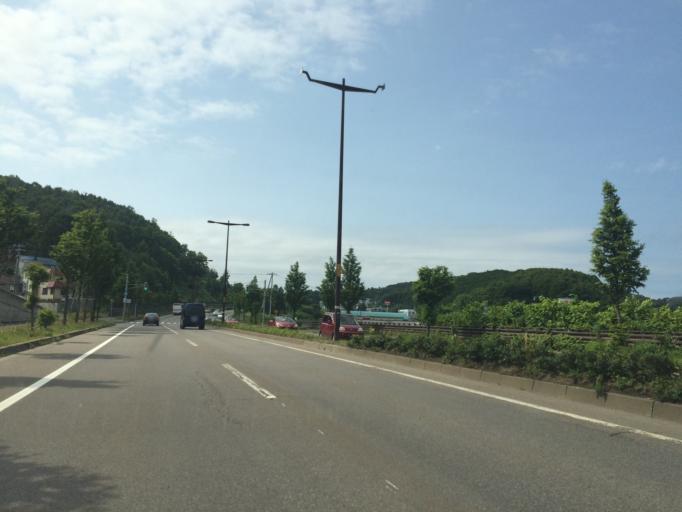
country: JP
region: Hokkaido
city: Otaru
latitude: 43.2130
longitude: 140.9603
